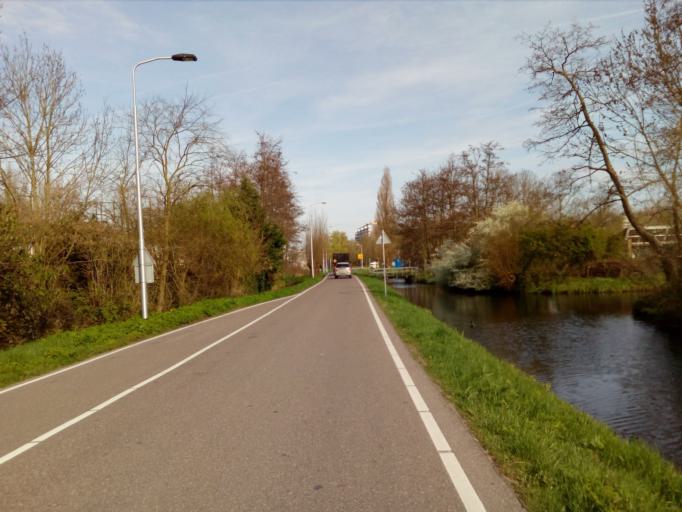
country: NL
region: South Holland
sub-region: Gemeente Delft
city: Delft
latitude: 51.9848
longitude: 4.3537
